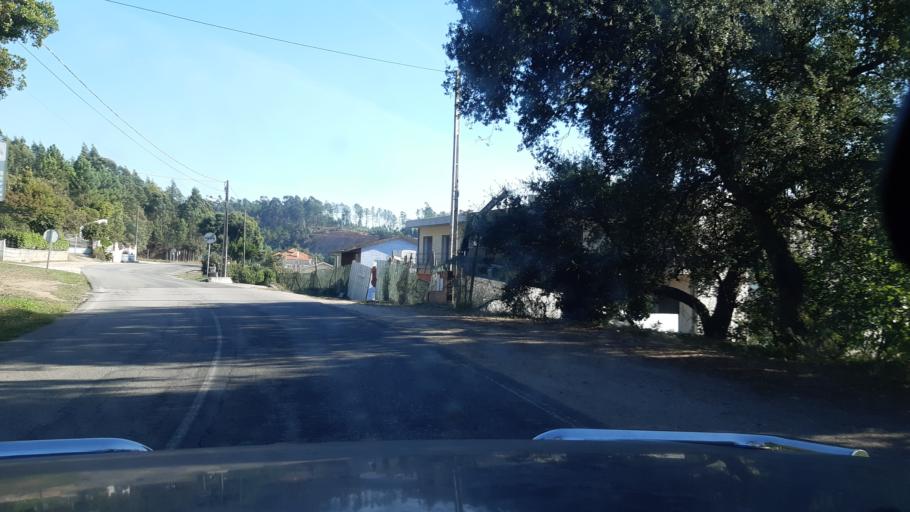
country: PT
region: Aveiro
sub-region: Agueda
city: Agueda
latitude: 40.5646
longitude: -8.4318
